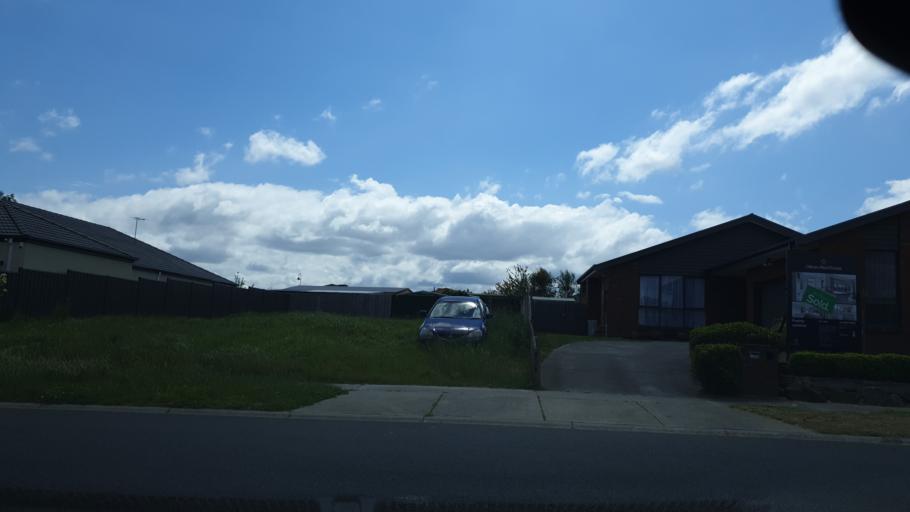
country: AU
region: Victoria
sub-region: Casey
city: Cranbourne North
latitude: -38.0768
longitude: 145.2894
